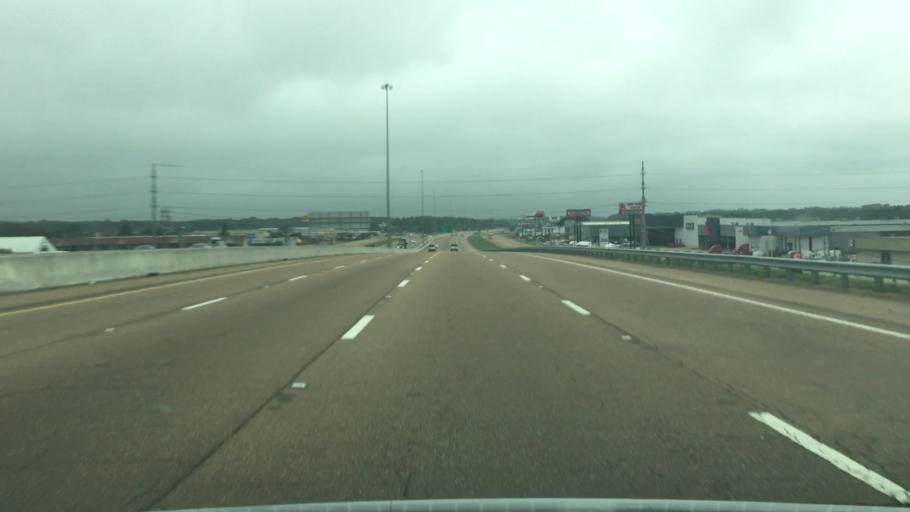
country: US
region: Mississippi
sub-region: Rankin County
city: Richland
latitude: 32.2634
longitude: -90.1609
